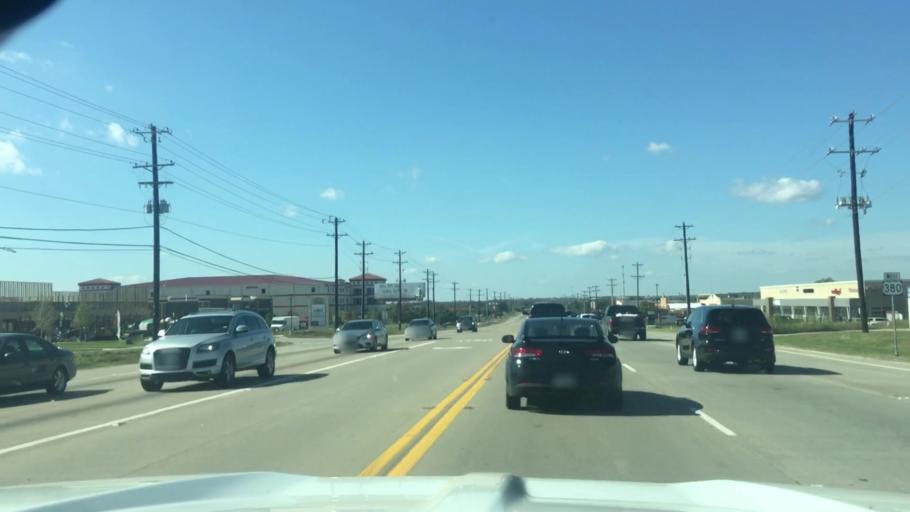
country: US
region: Texas
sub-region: Denton County
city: Little Elm
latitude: 33.2208
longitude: -96.9308
